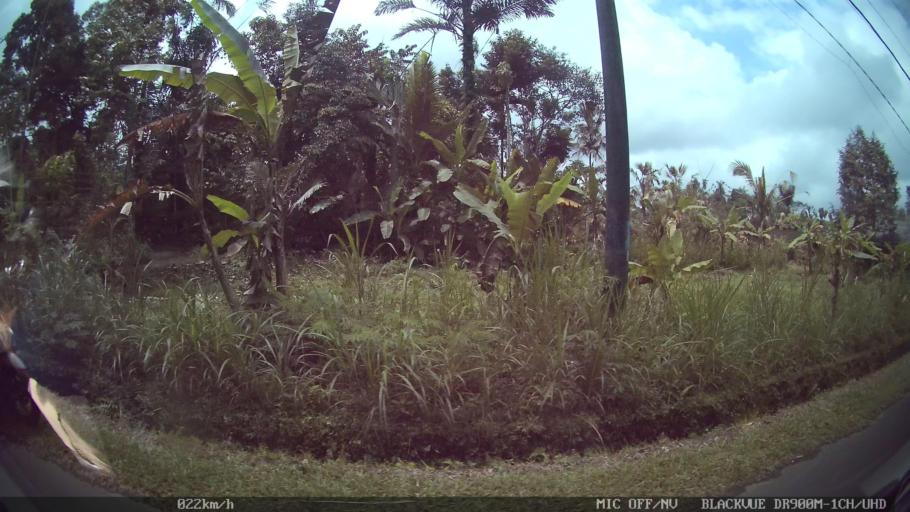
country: ID
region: Bali
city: Banjar Geriana Kangin
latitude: -8.3970
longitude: 115.4414
